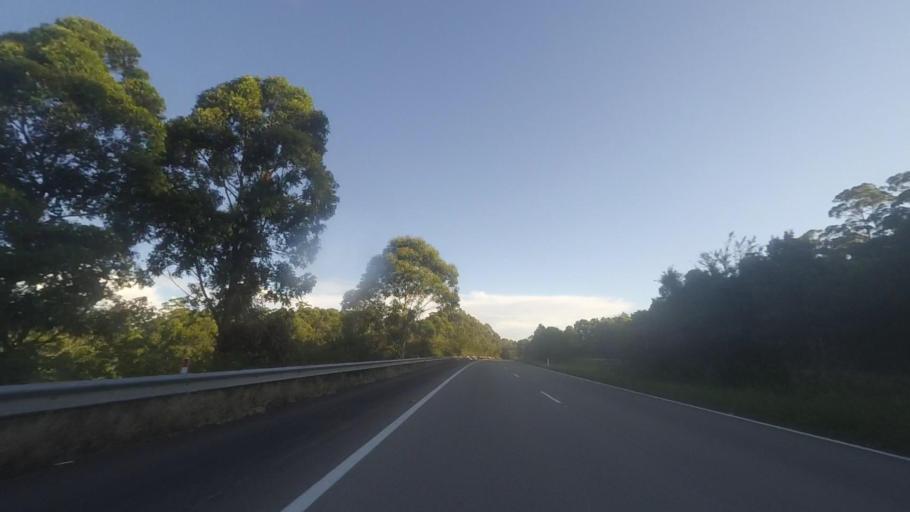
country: AU
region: New South Wales
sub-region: Great Lakes
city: Bulahdelah
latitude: -32.2990
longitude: 152.3460
